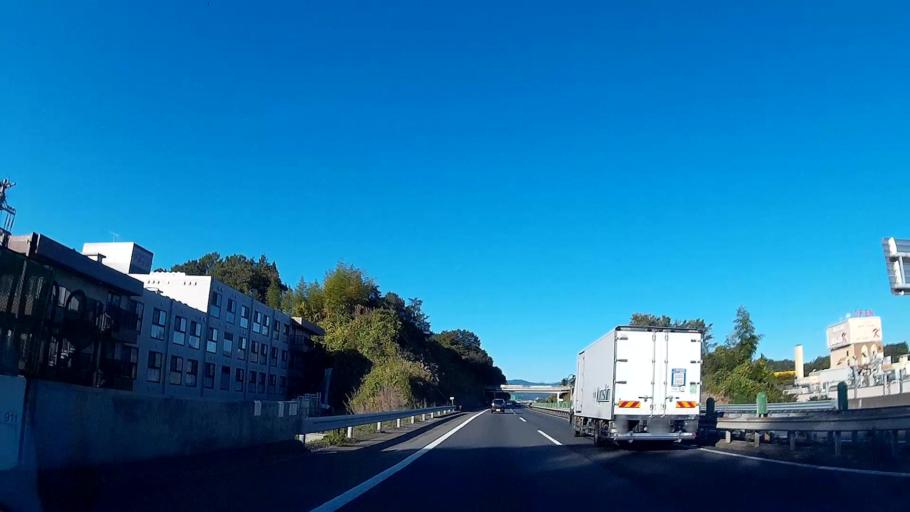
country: JP
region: Tokyo
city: Hachioji
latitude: 35.6767
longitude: 139.3319
